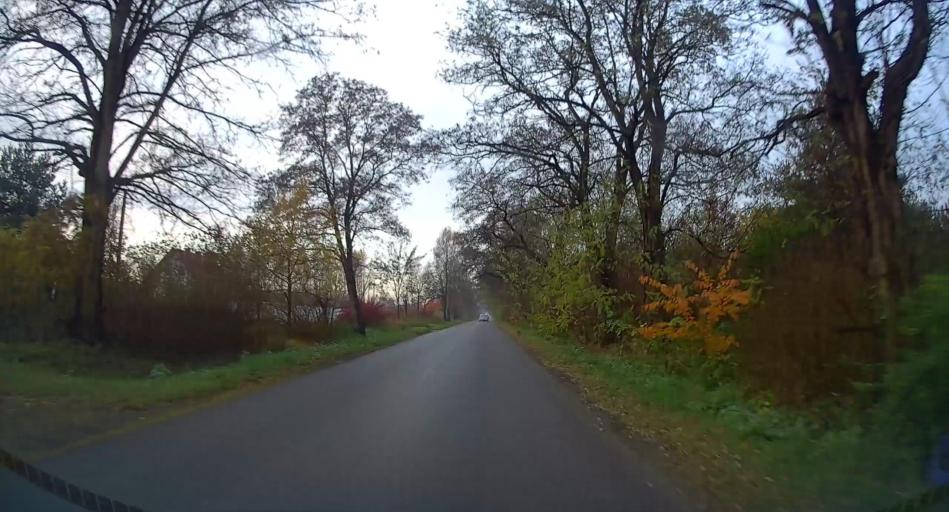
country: PL
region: Masovian Voivodeship
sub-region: Powiat zyrardowski
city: Puszcza Marianska
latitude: 51.9322
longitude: 20.3627
